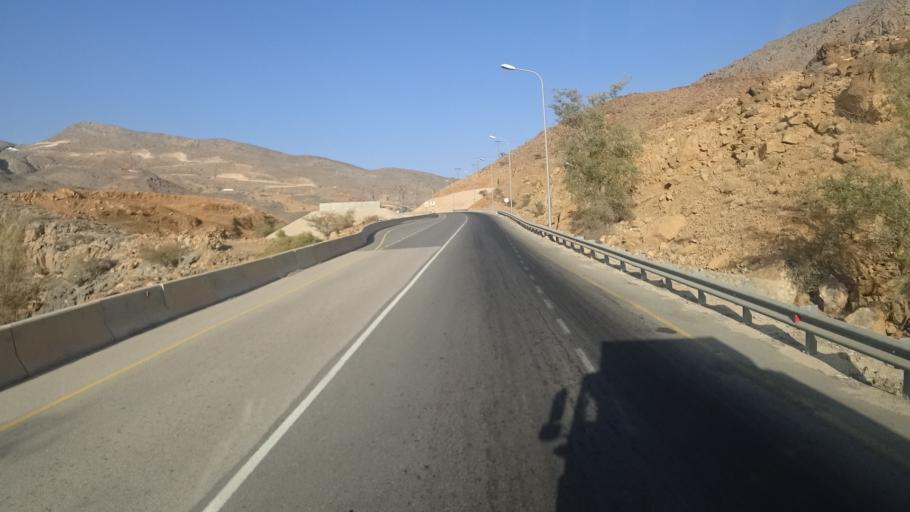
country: OM
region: Muhafazat ad Dakhiliyah
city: Izki
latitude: 22.9687
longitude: 57.6912
